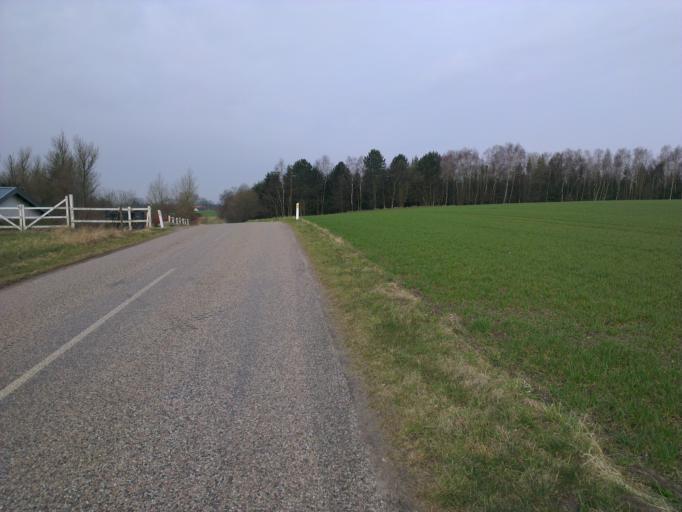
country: DK
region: Capital Region
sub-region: Frederikssund Kommune
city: Skibby
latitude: 55.7615
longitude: 11.8971
